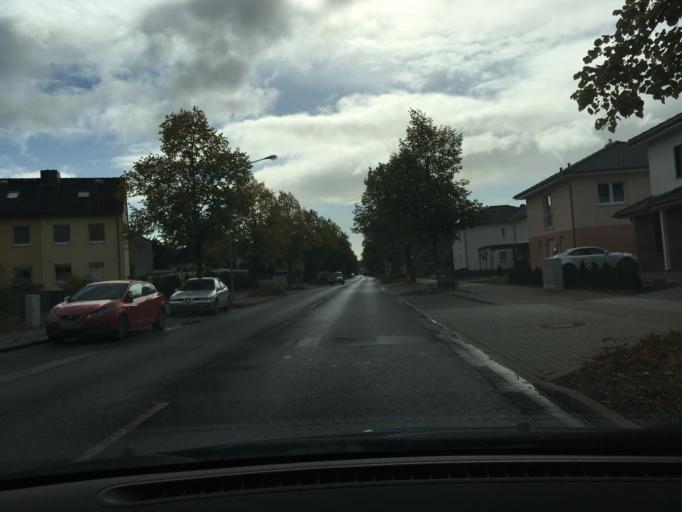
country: DE
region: Lower Saxony
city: Uelzen
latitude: 52.9712
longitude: 10.5714
